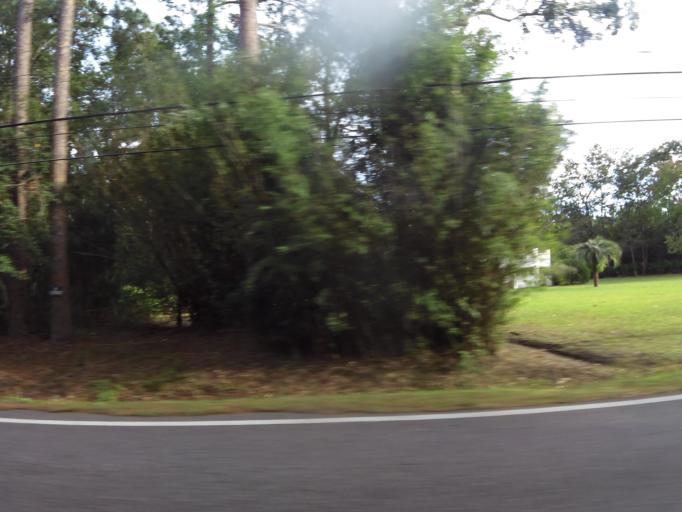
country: US
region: Florida
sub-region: Duval County
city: Jacksonville
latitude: 30.4482
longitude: -81.6882
